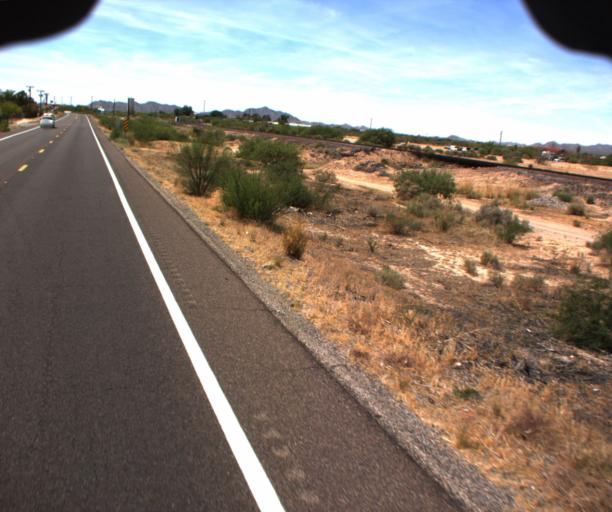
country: US
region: Arizona
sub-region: La Paz County
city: Salome
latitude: 33.7852
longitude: -113.6085
